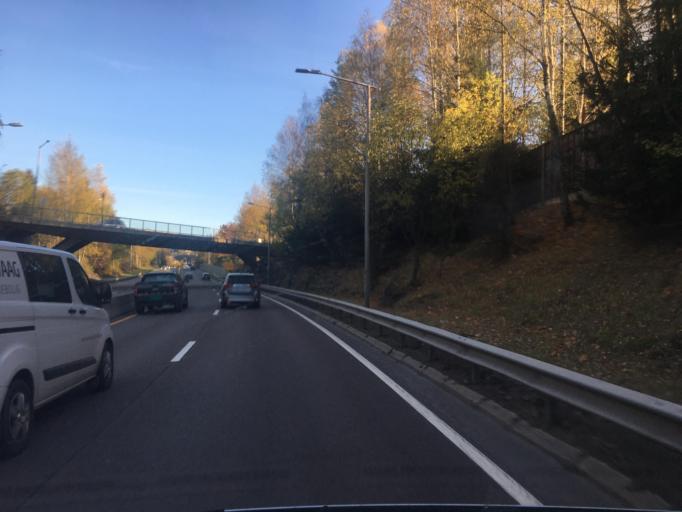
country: NO
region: Akershus
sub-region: Lorenskog
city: Kjenn
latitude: 59.9504
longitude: 10.9370
